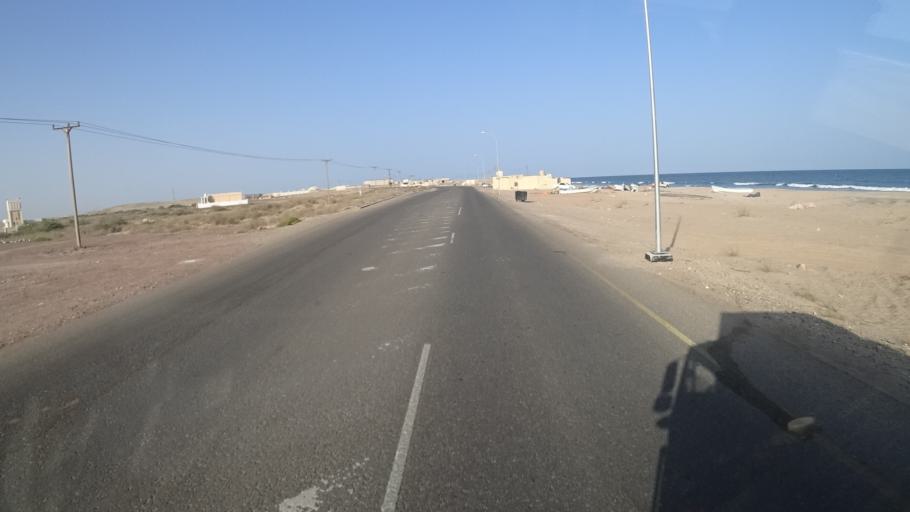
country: OM
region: Ash Sharqiyah
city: Sur
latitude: 22.1657
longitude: 59.7552
